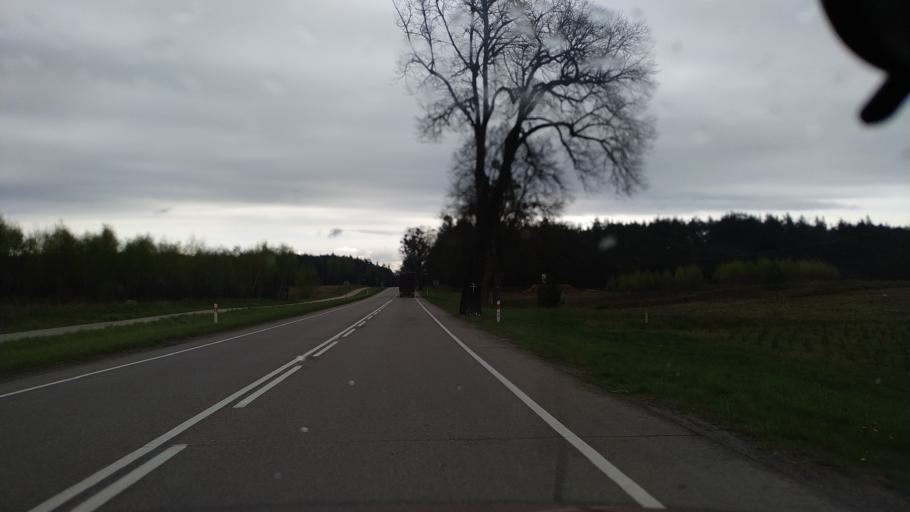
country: PL
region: Pomeranian Voivodeship
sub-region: Powiat starogardzki
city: Kaliska
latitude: 53.9058
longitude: 18.2535
